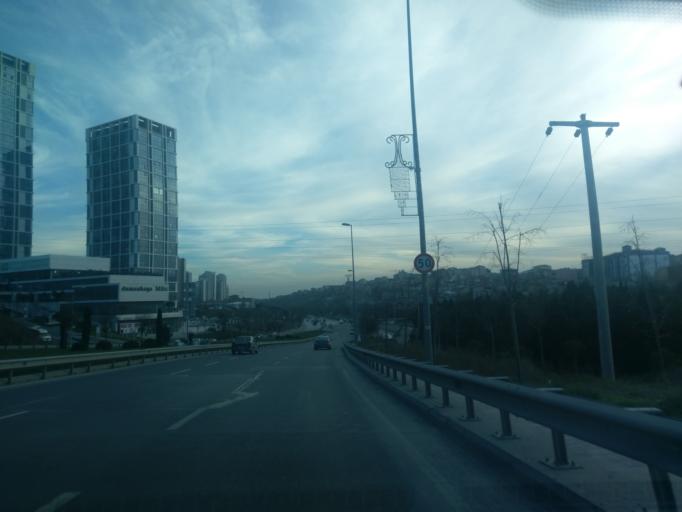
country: TR
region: Istanbul
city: Basaksehir
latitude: 41.0591
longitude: 28.7582
